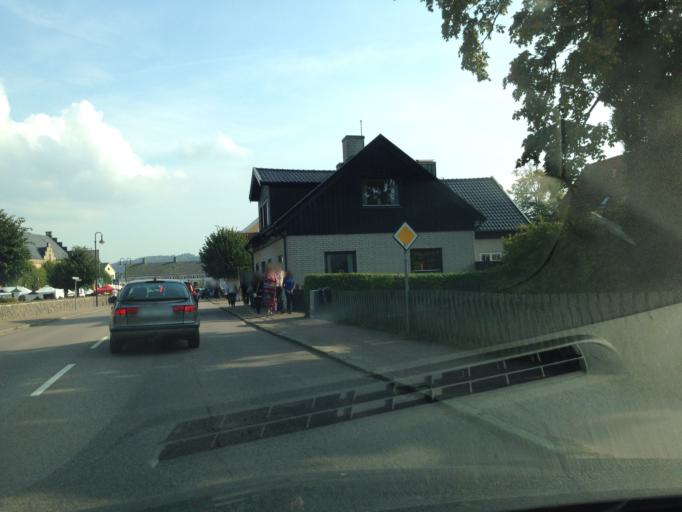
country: SE
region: Skane
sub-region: Bastads Kommun
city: Bastad
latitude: 56.4333
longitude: 12.8345
